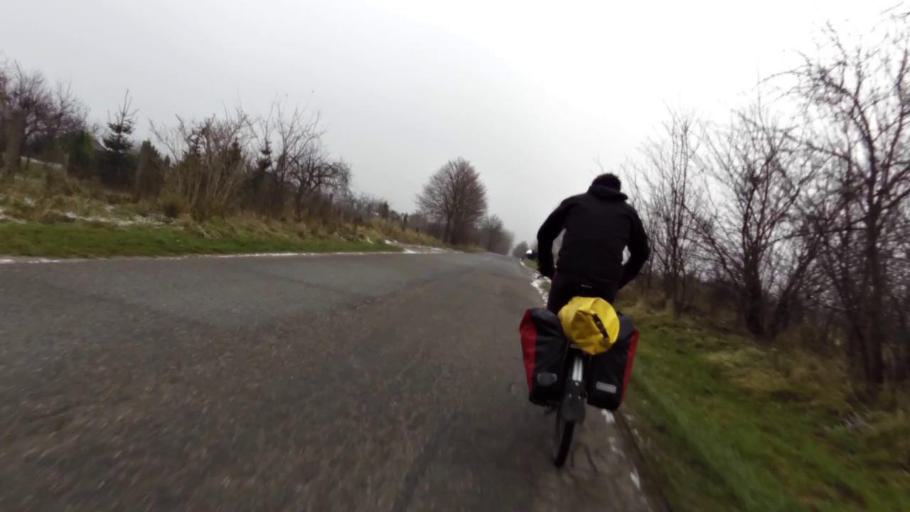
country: PL
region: West Pomeranian Voivodeship
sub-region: Powiat walecki
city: Walcz
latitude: 53.2894
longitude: 16.4747
